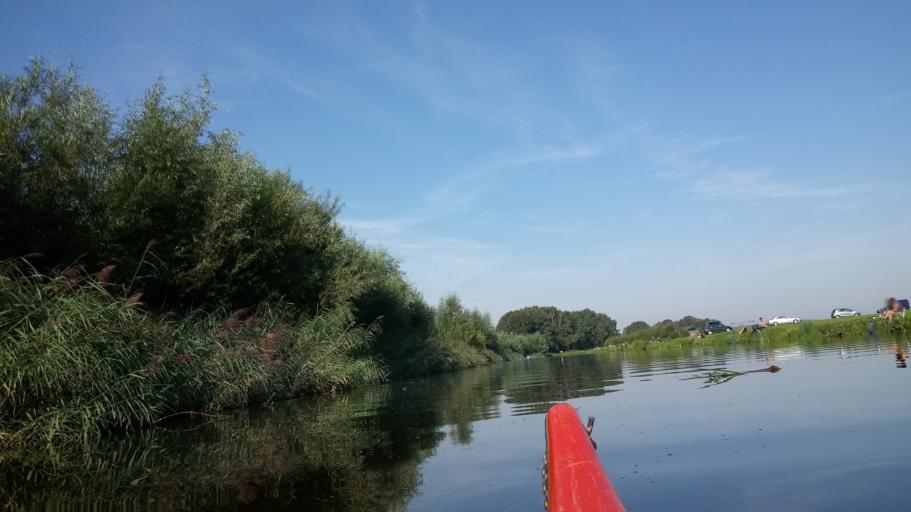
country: NL
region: Gelderland
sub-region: Berkelland
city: Borculo
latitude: 52.1298
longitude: 6.4940
